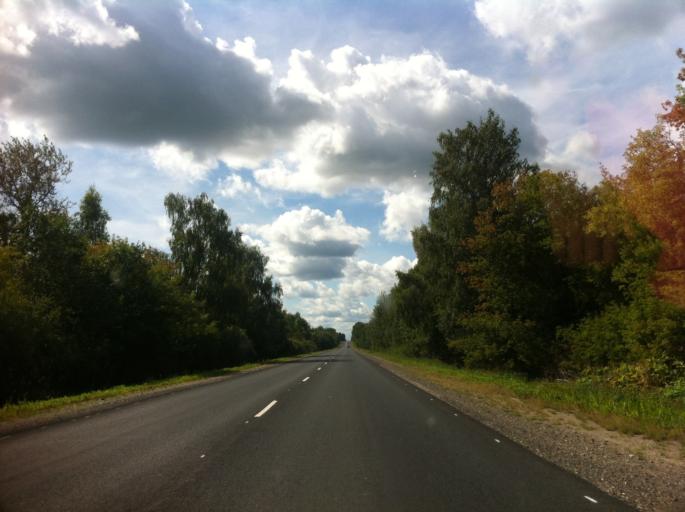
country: RU
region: Pskov
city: Izborsk
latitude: 57.7239
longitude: 27.9472
